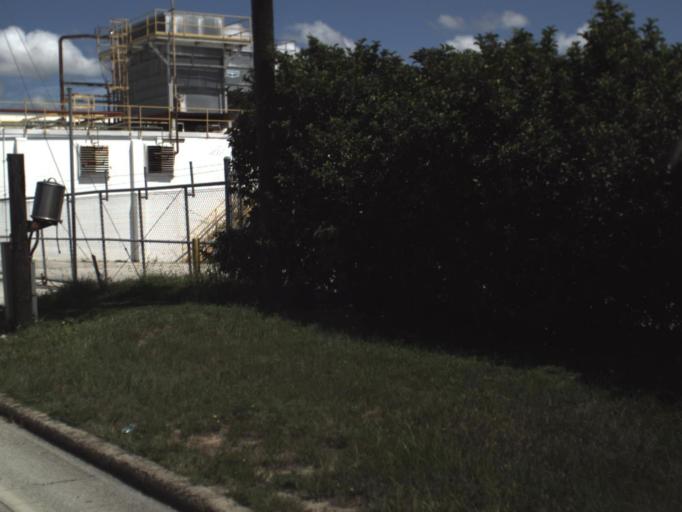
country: US
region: Florida
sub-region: Polk County
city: Frostproof
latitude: 27.7398
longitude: -81.5305
